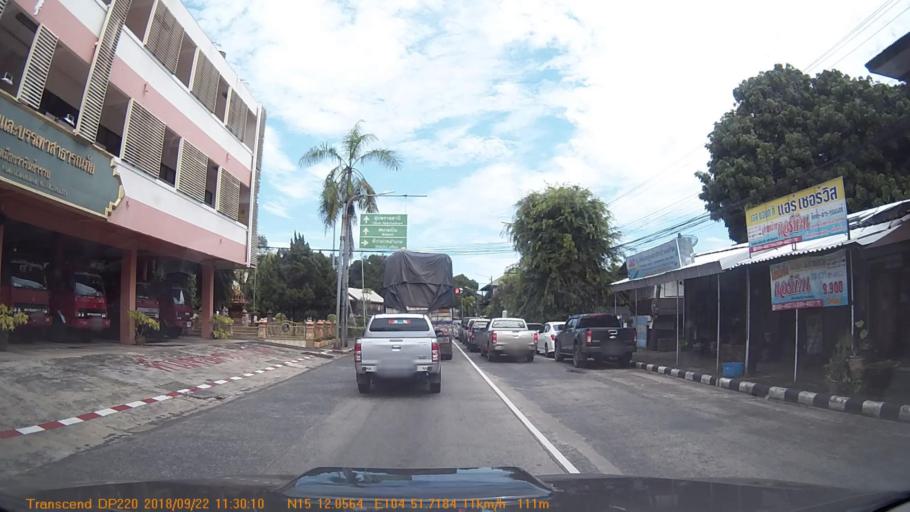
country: TH
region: Changwat Ubon Ratchathani
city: Warin Chamrap
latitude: 15.2011
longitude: 104.8620
